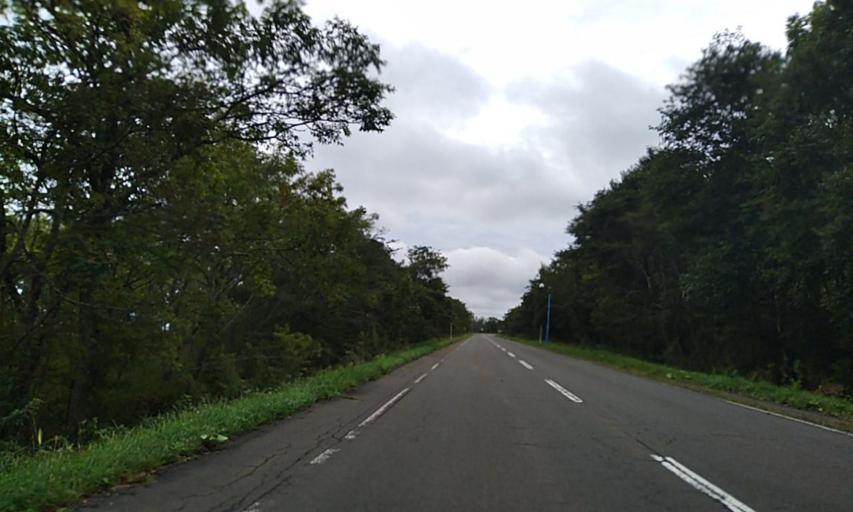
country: JP
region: Hokkaido
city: Shibetsu
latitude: 43.5183
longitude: 145.2431
